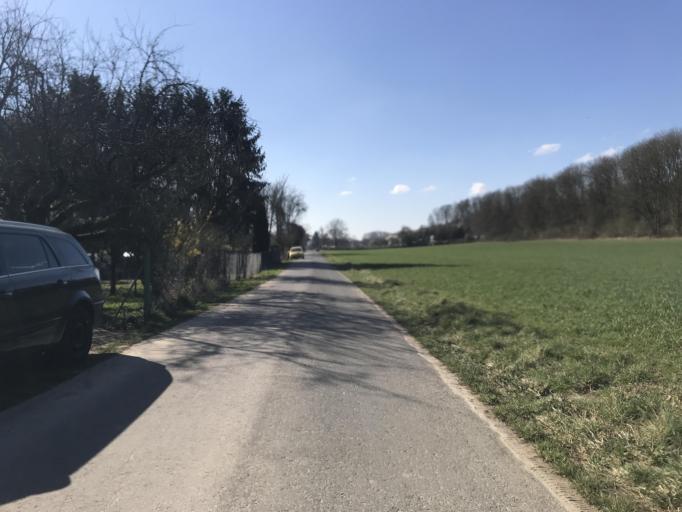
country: DE
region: Hesse
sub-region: Regierungsbezirk Darmstadt
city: Florsheim
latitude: 50.0099
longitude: 8.4071
